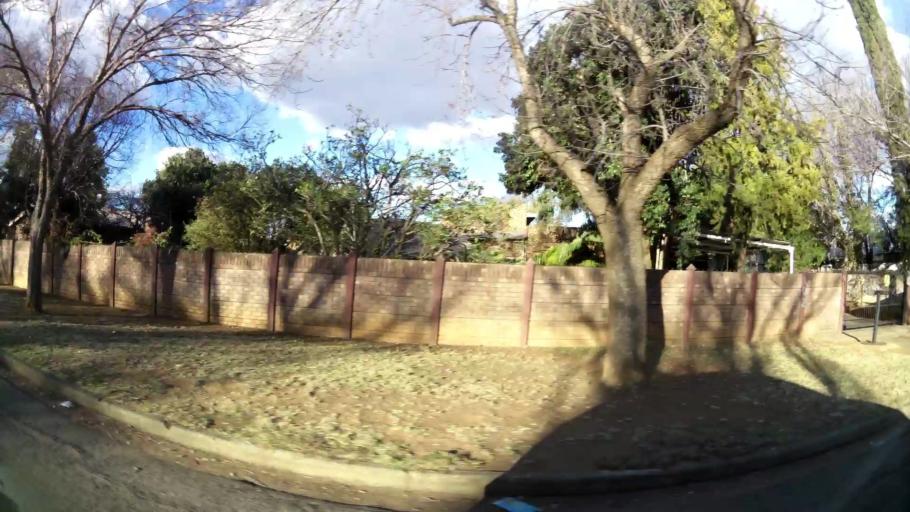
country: ZA
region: North-West
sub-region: Dr Kenneth Kaunda District Municipality
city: Potchefstroom
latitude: -26.7320
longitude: 27.0841
